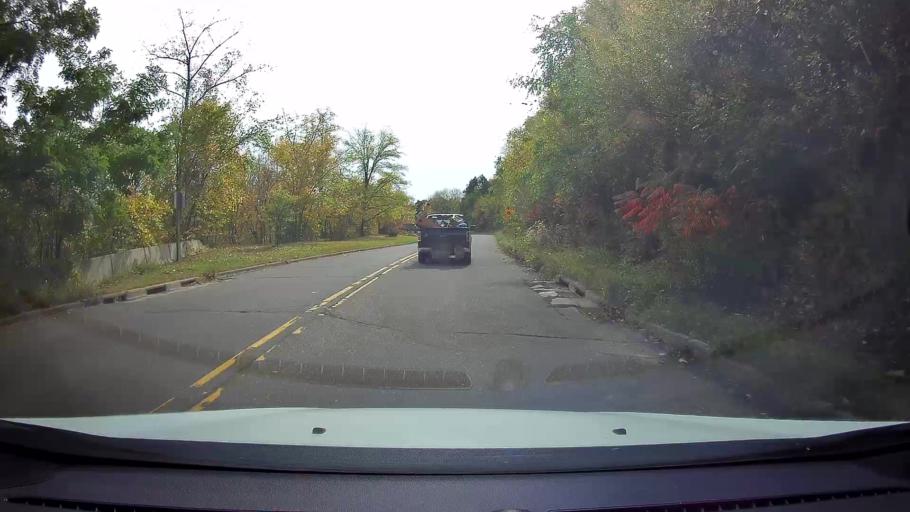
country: US
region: Wisconsin
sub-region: Polk County
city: Osceola
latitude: 45.3200
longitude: -92.7077
